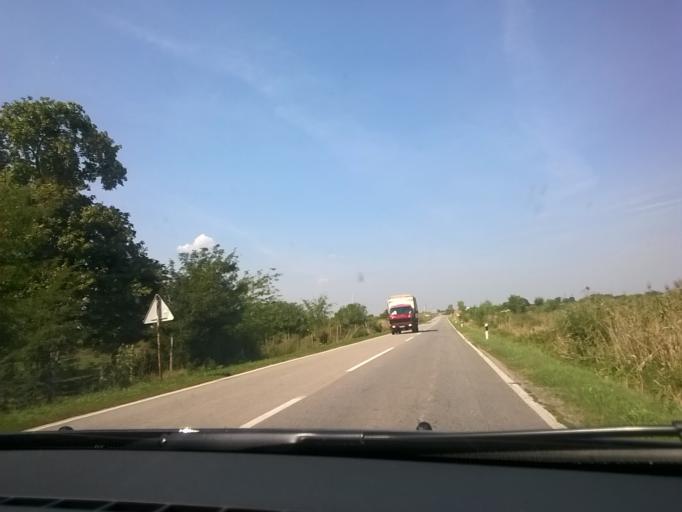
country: RS
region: Autonomna Pokrajina Vojvodina
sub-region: Juznobanatski Okrug
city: Vrsac
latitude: 45.1261
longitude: 21.2746
